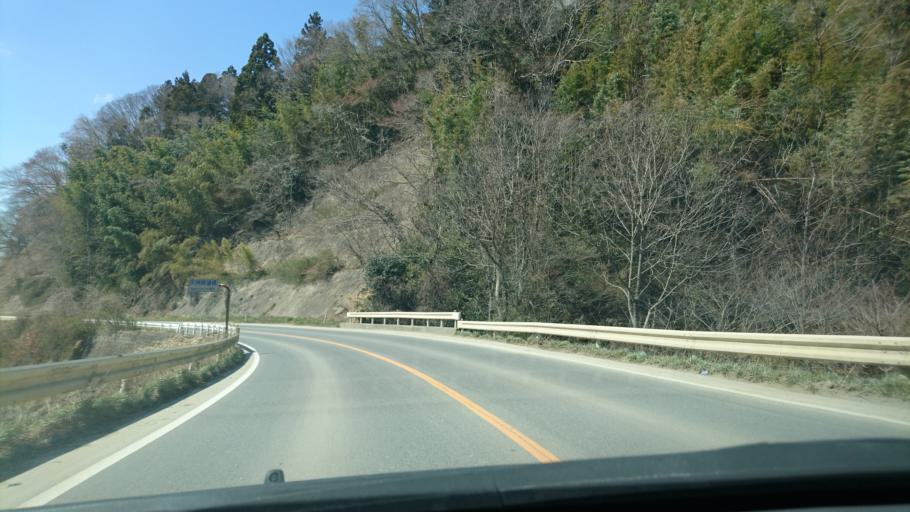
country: JP
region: Miyagi
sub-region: Oshika Gun
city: Onagawa Cho
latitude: 38.5358
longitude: 141.4344
